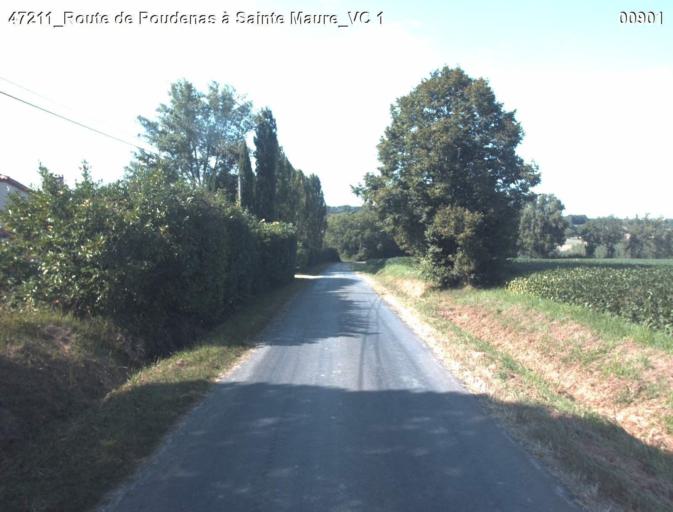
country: FR
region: Aquitaine
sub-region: Departement du Lot-et-Garonne
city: Mezin
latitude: 44.0398
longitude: 0.2096
